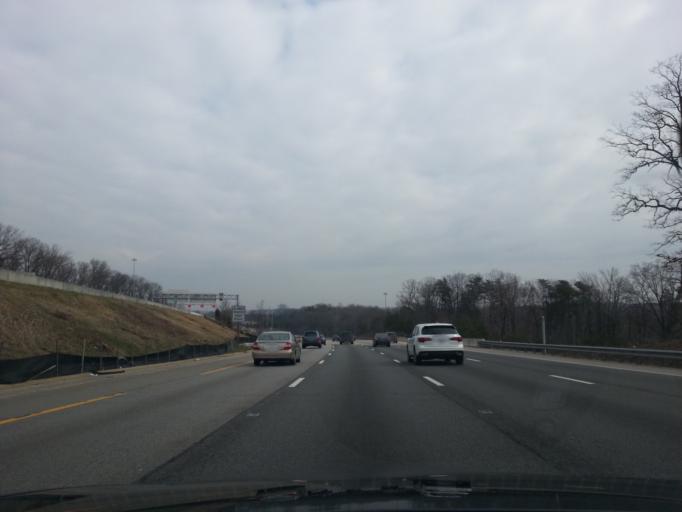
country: US
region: Virginia
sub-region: Fairfax County
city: Lorton
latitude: 38.6796
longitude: -77.2312
